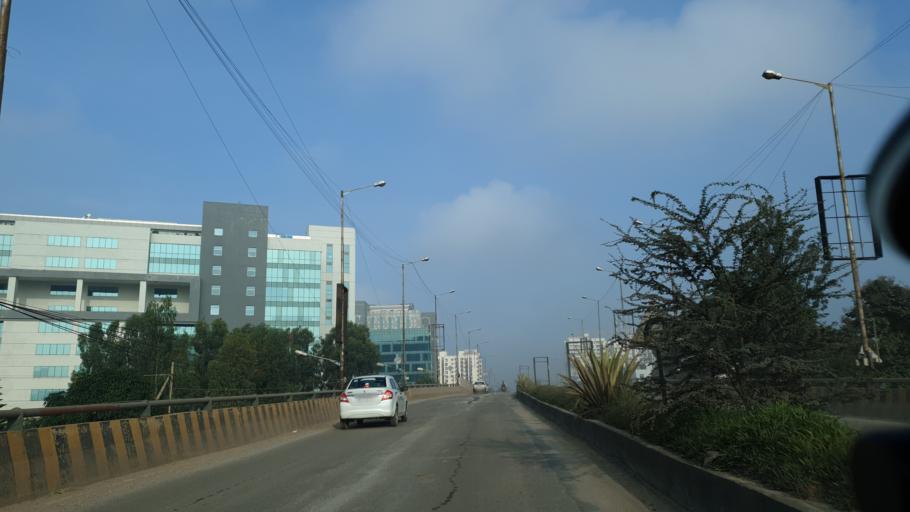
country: IN
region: Karnataka
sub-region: Bangalore Urban
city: Bangalore
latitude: 12.9017
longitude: 77.7073
